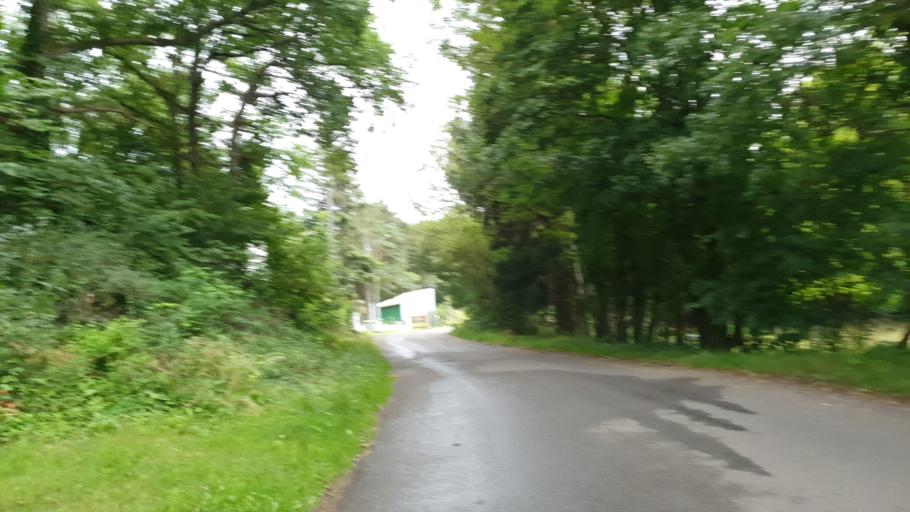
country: FR
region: Auvergne
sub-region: Departement du Puy-de-Dome
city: Aydat
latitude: 45.5714
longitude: 3.0136
